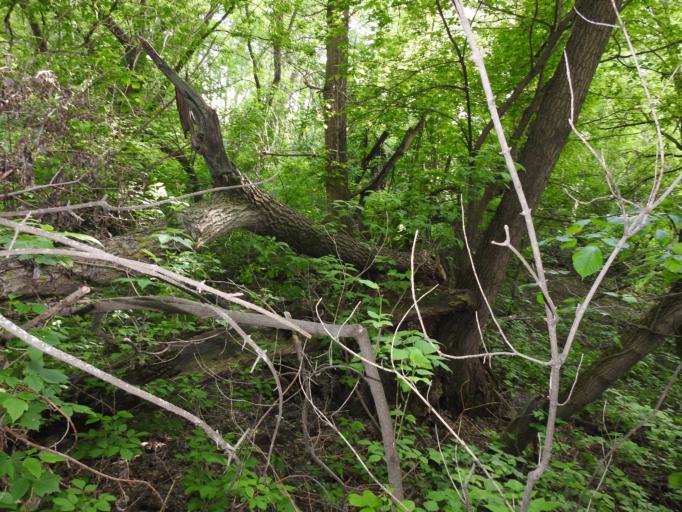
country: RU
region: Saratov
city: Engel's
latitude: 51.4684
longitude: 46.0763
